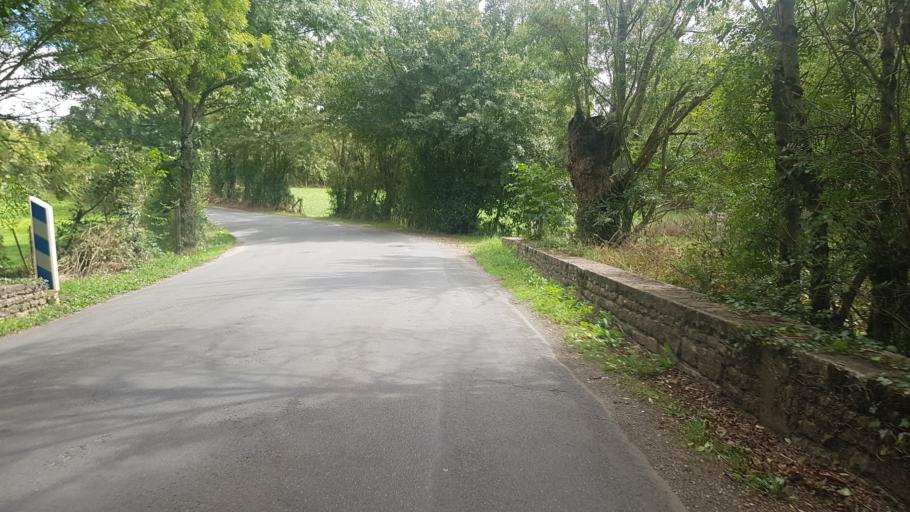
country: FR
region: Poitou-Charentes
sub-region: Departement des Deux-Sevres
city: Vouille
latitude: 46.3311
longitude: -0.3644
